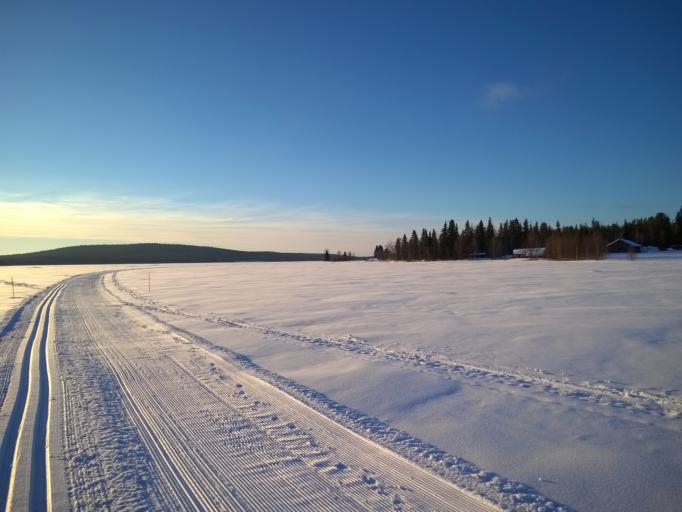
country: FI
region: Lapland
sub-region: Tunturi-Lappi
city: Muonio
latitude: 67.9204
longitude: 24.0542
